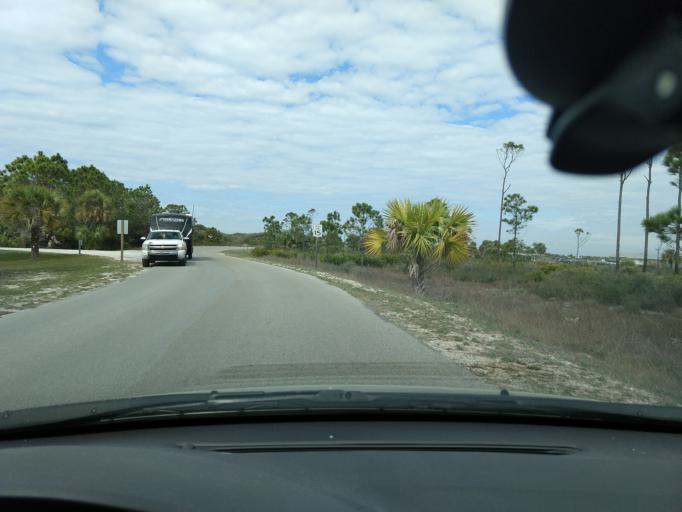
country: US
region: Florida
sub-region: Gulf County
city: Port Saint Joe
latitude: 29.7624
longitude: -85.4021
